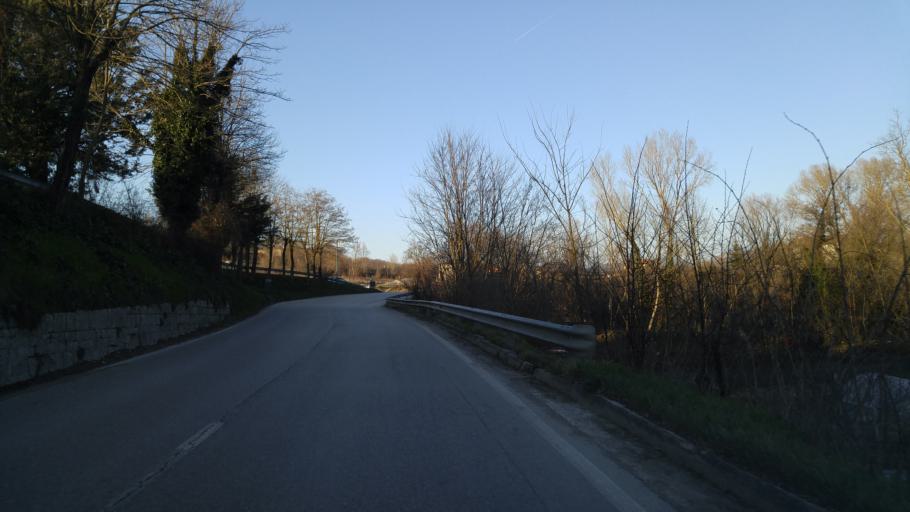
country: IT
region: The Marches
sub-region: Provincia di Pesaro e Urbino
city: Cagli
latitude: 43.5597
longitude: 12.6543
